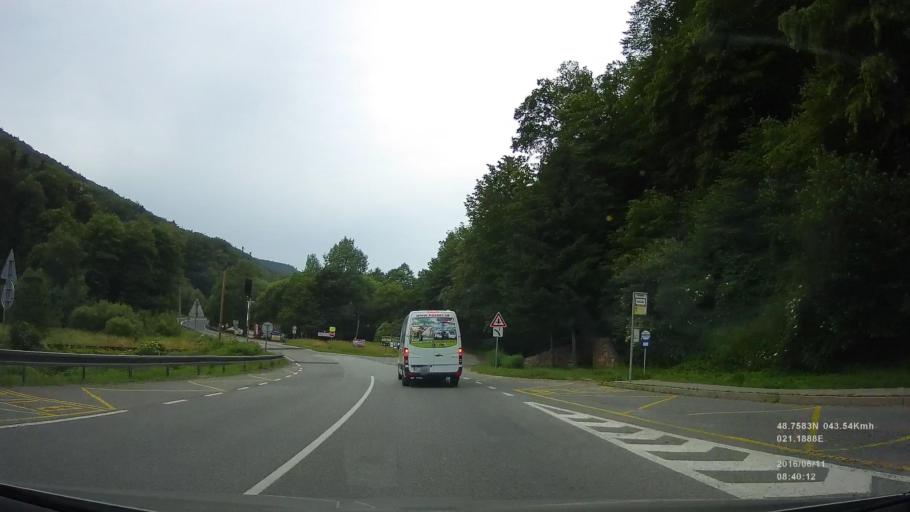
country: SK
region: Kosicky
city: Kosice
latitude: 48.7390
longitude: 21.2454
